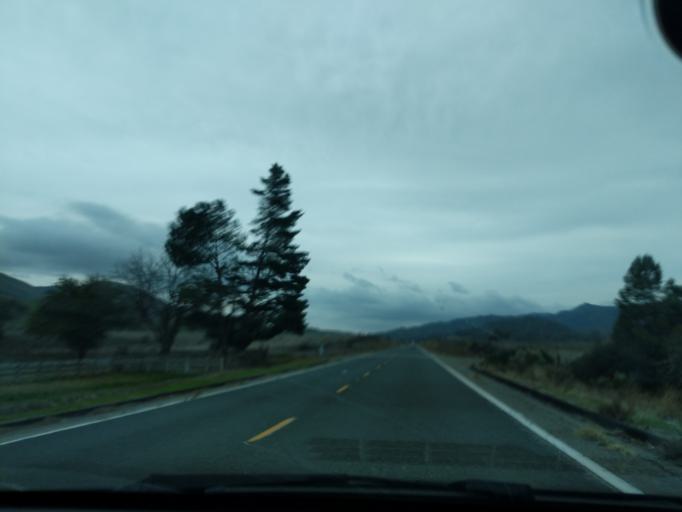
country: US
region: California
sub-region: San Benito County
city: Ridgemark
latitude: 36.6452
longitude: -121.2354
